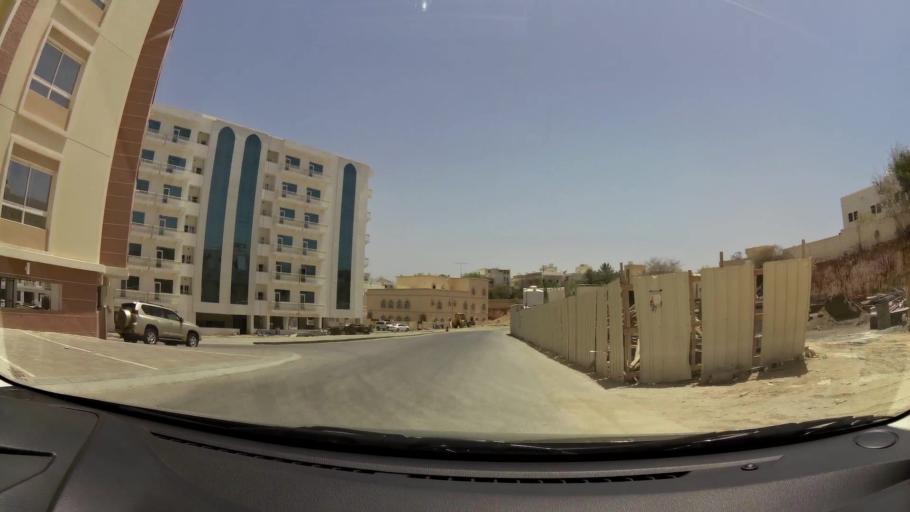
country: OM
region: Muhafazat Masqat
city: Muscat
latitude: 23.6220
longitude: 58.5008
